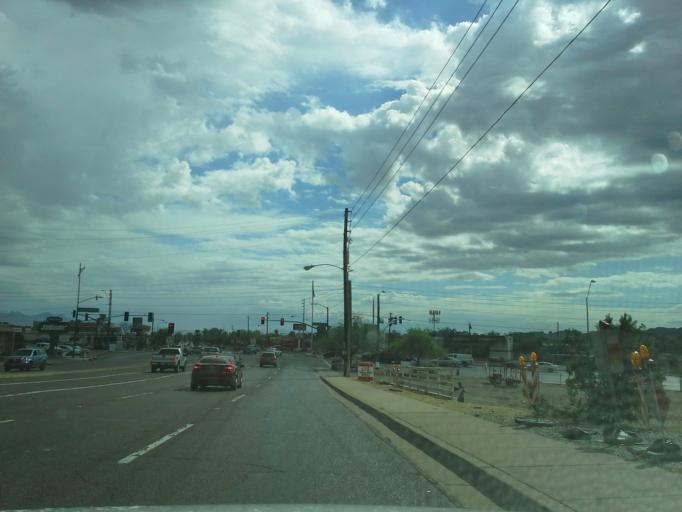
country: US
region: Arizona
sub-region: Maricopa County
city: Paradise Valley
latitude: 33.5969
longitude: -112.0392
